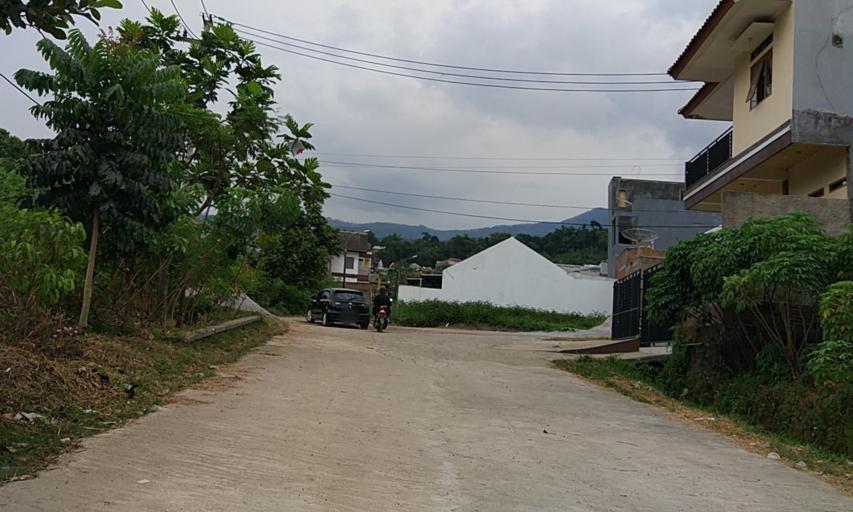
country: ID
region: West Java
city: Cileunyi
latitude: -6.8996
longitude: 107.6946
